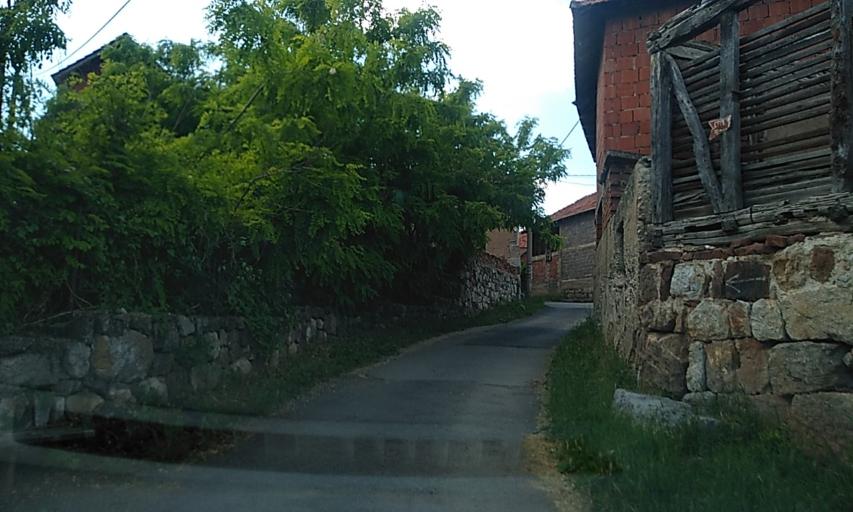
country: RS
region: Central Serbia
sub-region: Nisavski Okrug
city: Niska Banja
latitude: 43.3674
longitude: 22.0000
